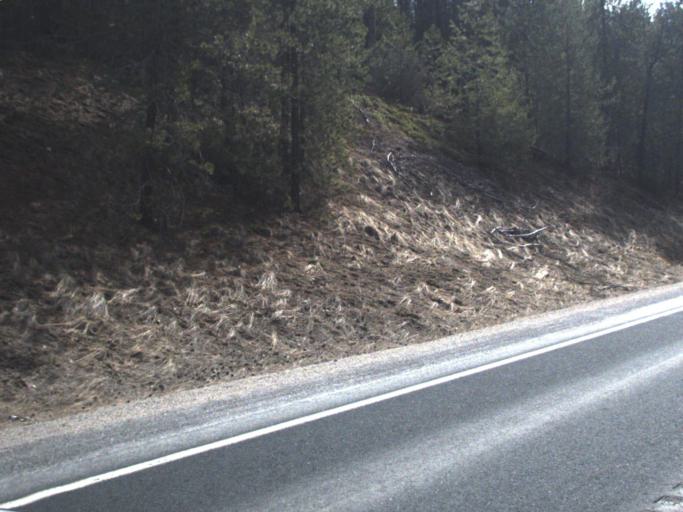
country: US
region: Washington
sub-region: Stevens County
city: Colville
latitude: 48.5080
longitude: -117.6745
